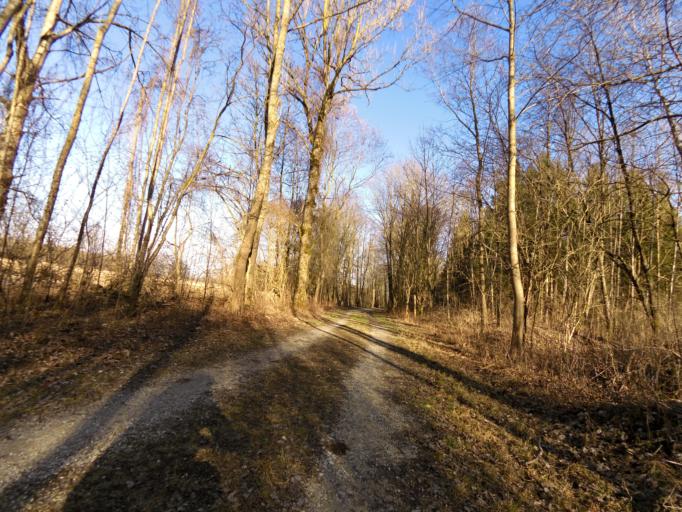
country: DE
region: Bavaria
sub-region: Lower Bavaria
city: Tiefenbach
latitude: 48.5181
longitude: 12.0973
